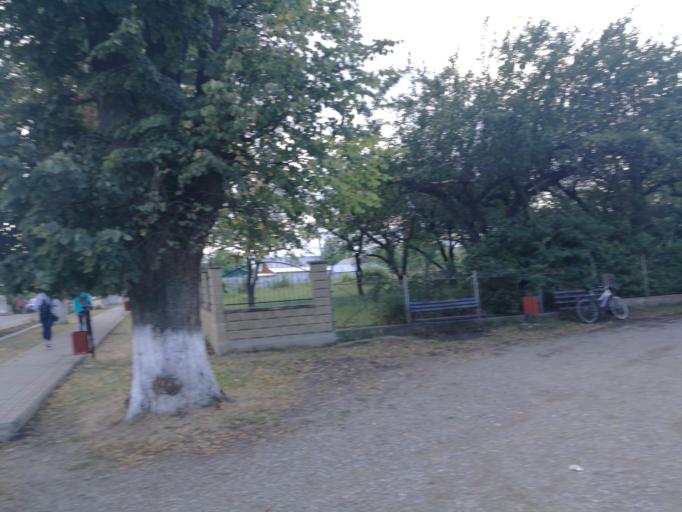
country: RO
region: Suceava
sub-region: Comuna Patrauti
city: Patrauti
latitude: 47.7162
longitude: 26.1899
